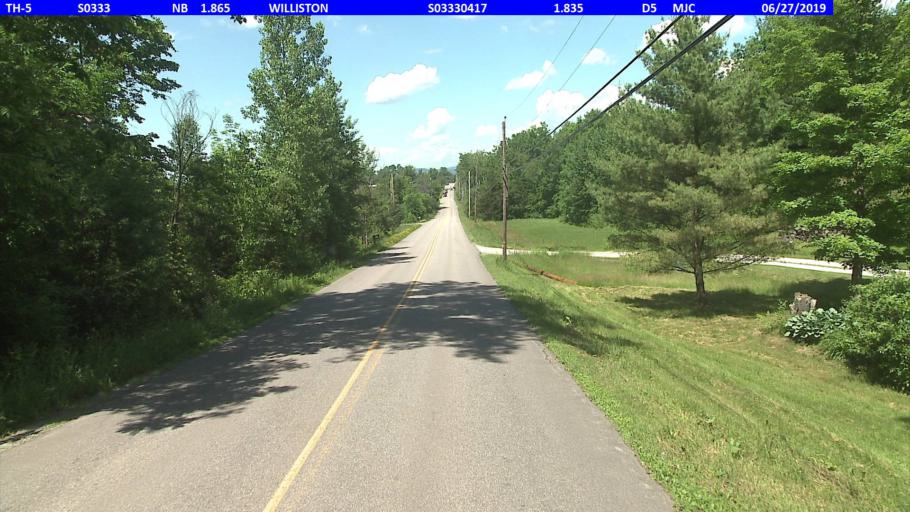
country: US
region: Vermont
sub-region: Chittenden County
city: South Burlington
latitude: 44.4275
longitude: -73.1337
